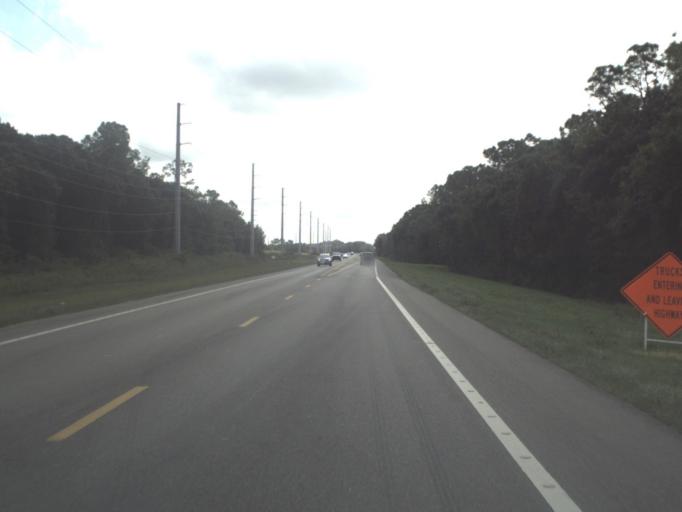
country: US
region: Florida
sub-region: Sarasota County
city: The Meadows
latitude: 27.4247
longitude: -82.3730
